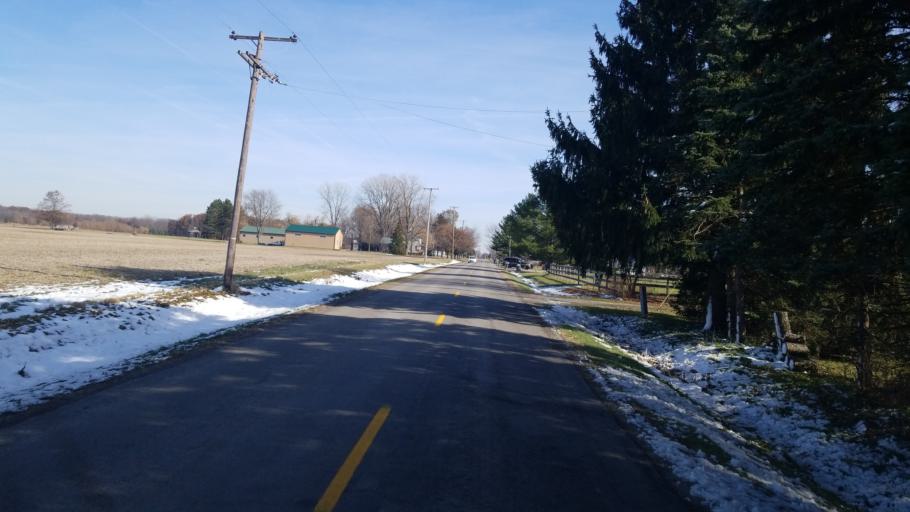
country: US
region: Ohio
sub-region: Huron County
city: Wakeman
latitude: 41.2037
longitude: -82.5051
